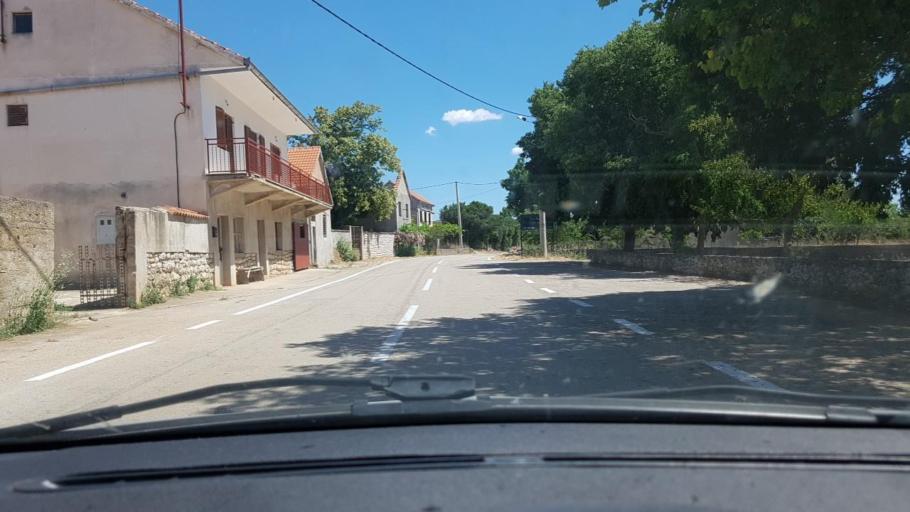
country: HR
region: Sibensko-Kniniska
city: Kistanje
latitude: 43.8875
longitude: 15.9108
